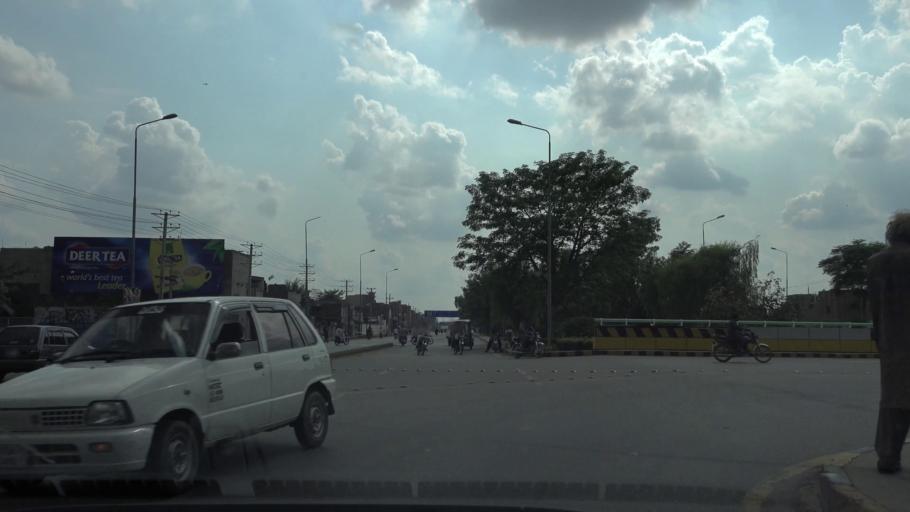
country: PK
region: Punjab
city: Faisalabad
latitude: 31.4220
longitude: 73.1090
